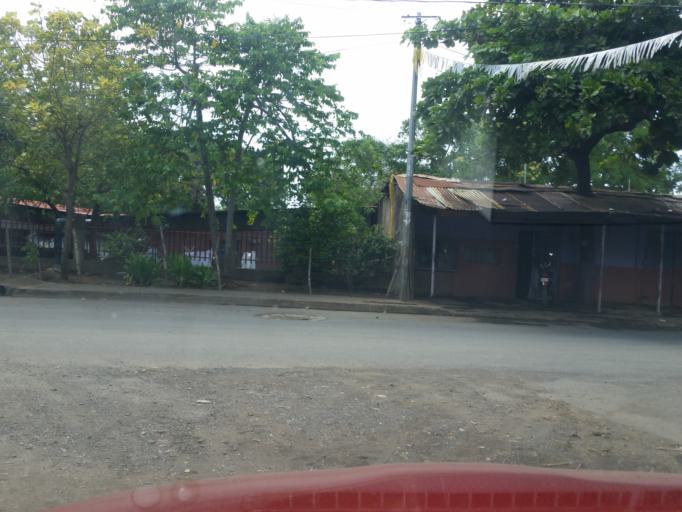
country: NI
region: Managua
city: Managua
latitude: 12.1053
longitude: -86.2290
